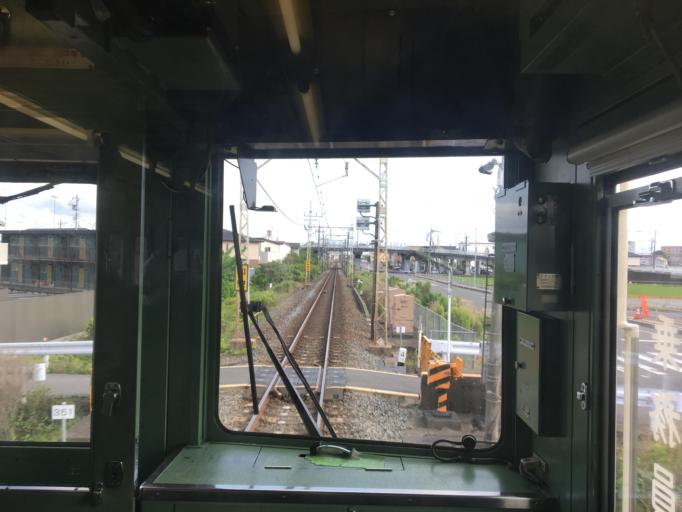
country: JP
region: Tochigi
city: Ashikaga
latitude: 36.3189
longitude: 139.4542
